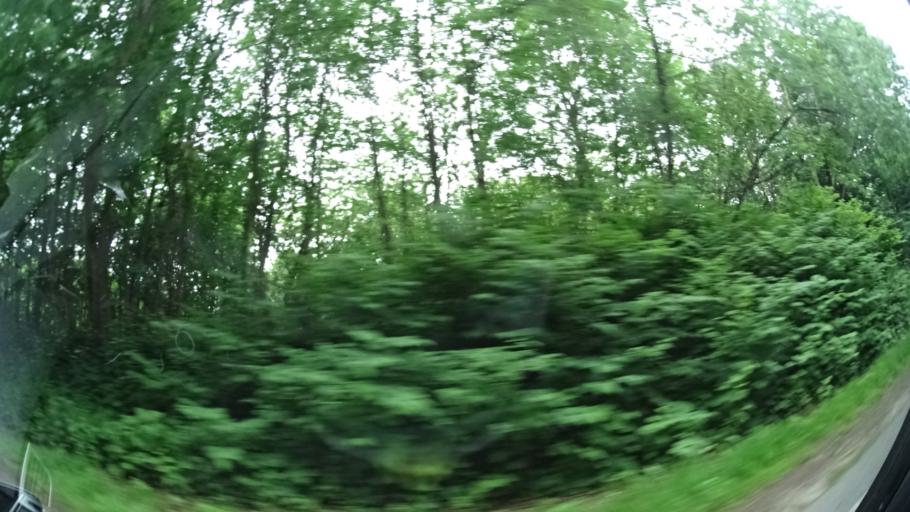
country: DK
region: Central Jutland
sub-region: Syddjurs Kommune
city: Hornslet
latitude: 56.3022
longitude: 10.3783
